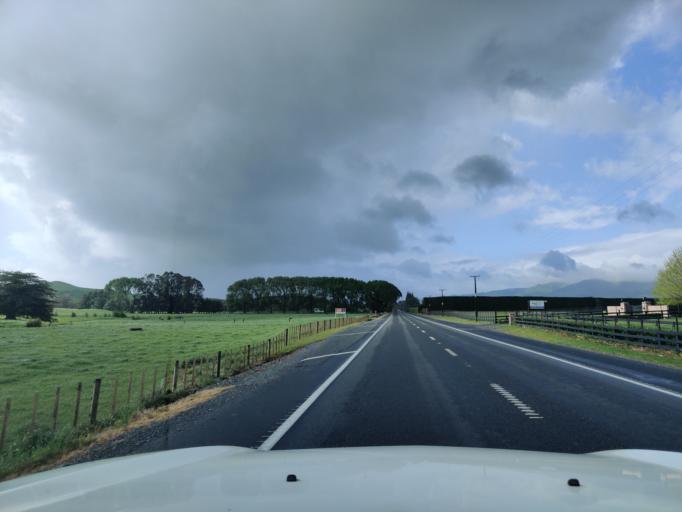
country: NZ
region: Waikato
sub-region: Waipa District
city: Cambridge
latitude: -37.9312
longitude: 175.5721
